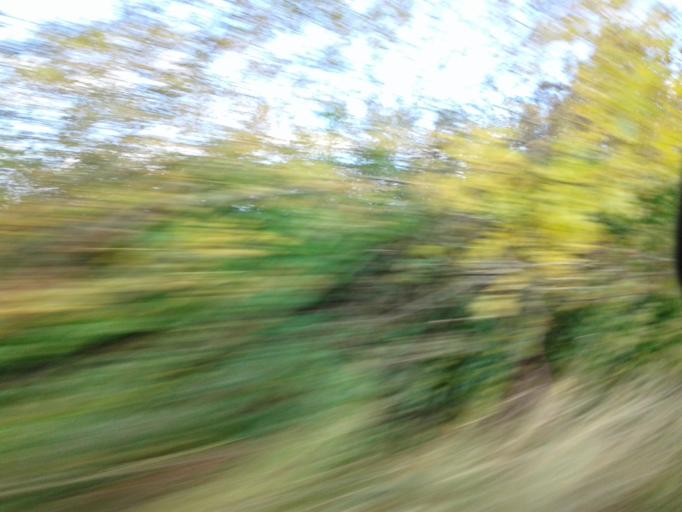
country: IE
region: Leinster
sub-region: An Mhi
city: Slane
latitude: 53.6874
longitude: -6.5130
